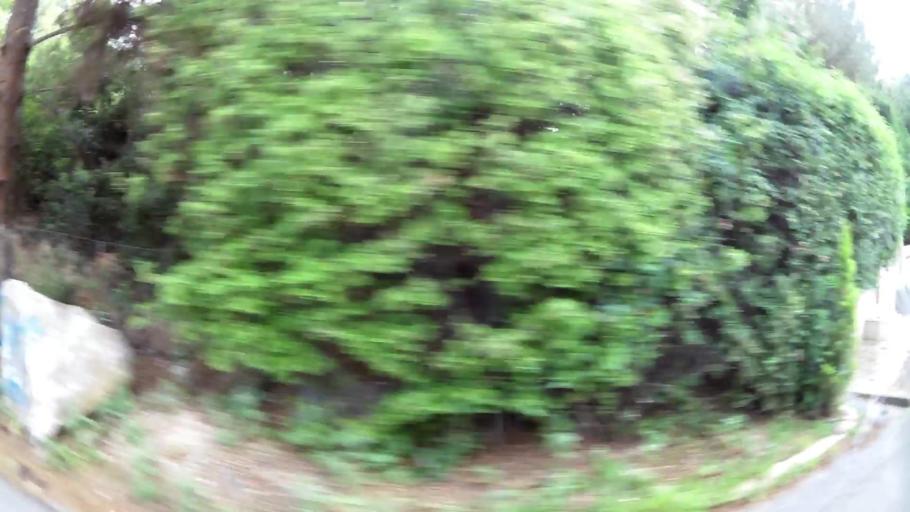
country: GR
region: Central Macedonia
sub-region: Nomos Thessalonikis
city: Panorama
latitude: 40.5886
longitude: 23.0164
